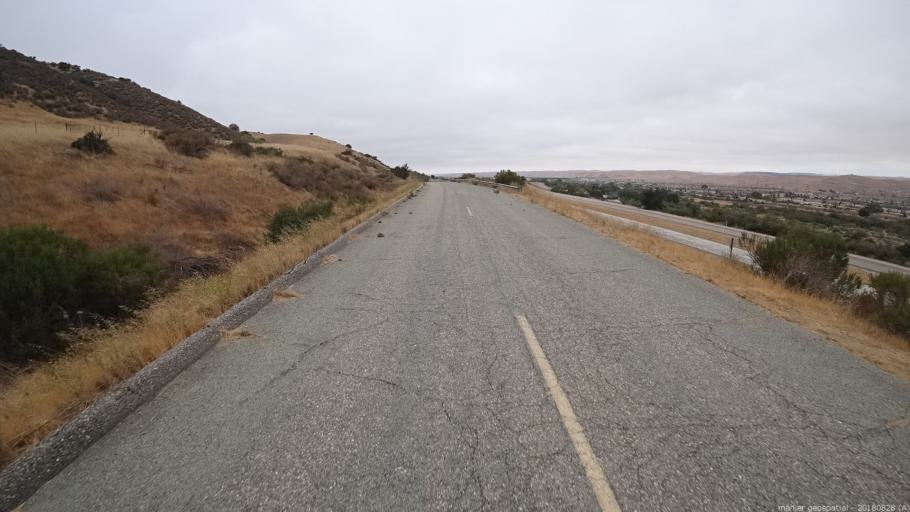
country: US
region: California
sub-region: San Luis Obispo County
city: Lake Nacimiento
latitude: 35.9432
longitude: -120.8752
